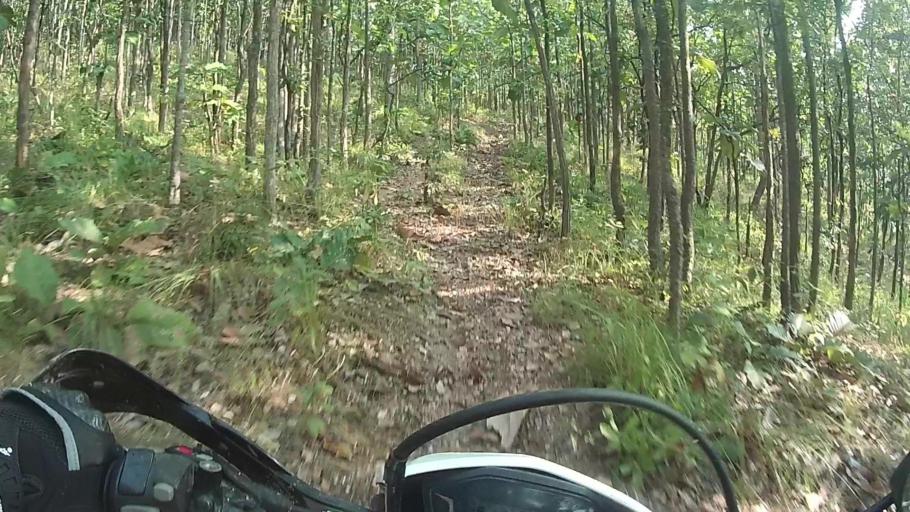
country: TH
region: Chiang Mai
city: San Sai
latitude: 18.9438
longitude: 99.0579
